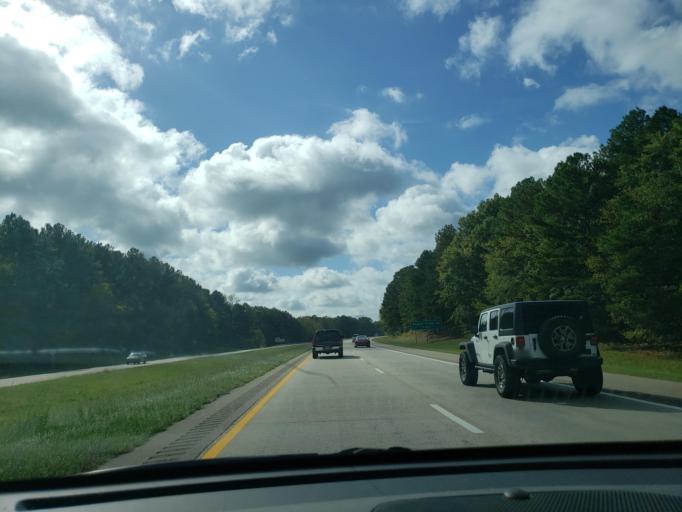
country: US
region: North Carolina
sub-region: Vance County
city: South Henderson
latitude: 36.3202
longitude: -78.4662
